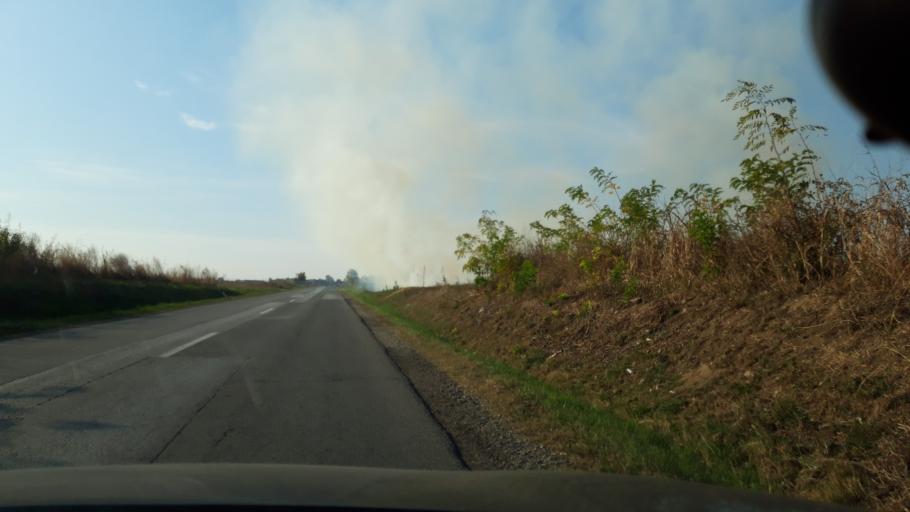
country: RS
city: Putinci
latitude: 44.9973
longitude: 19.9530
